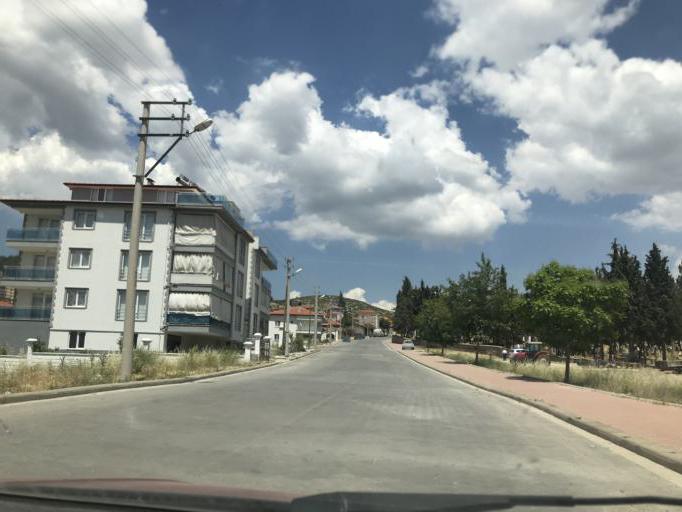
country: TR
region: Denizli
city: Tavas
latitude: 37.5731
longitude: 29.0632
